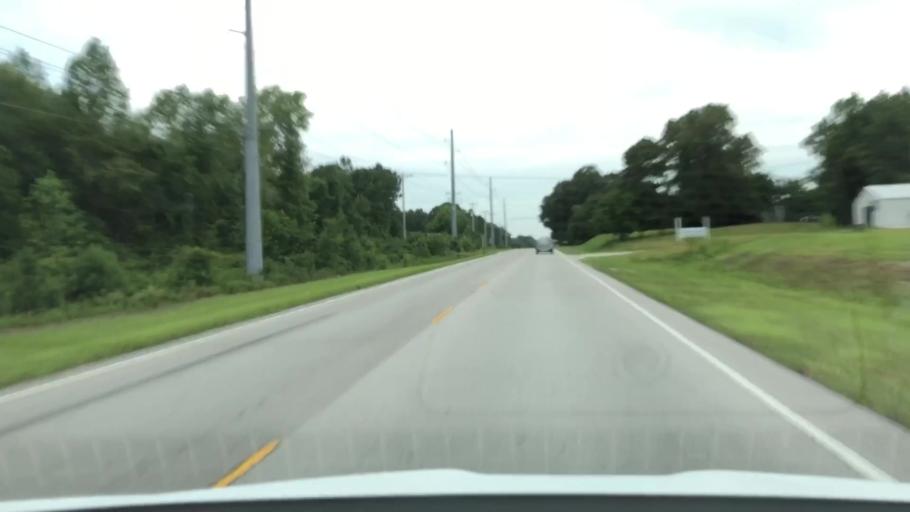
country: US
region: North Carolina
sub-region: Carteret County
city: Cape Carteret
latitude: 34.7534
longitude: -77.0932
